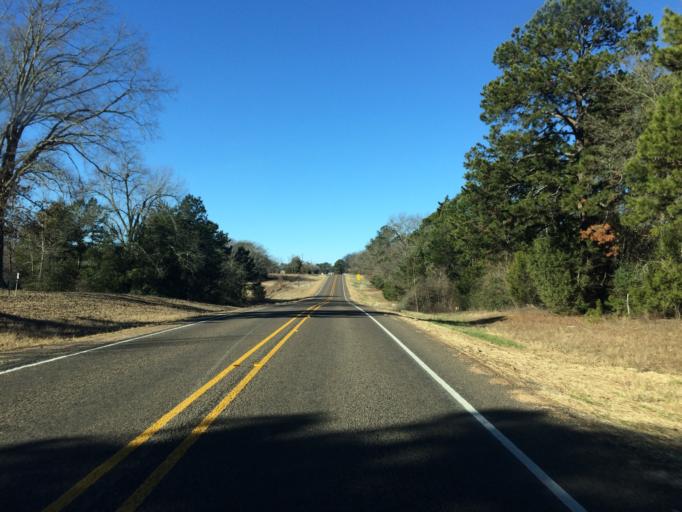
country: US
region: Texas
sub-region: Wood County
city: Hawkins
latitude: 32.6346
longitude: -95.2663
